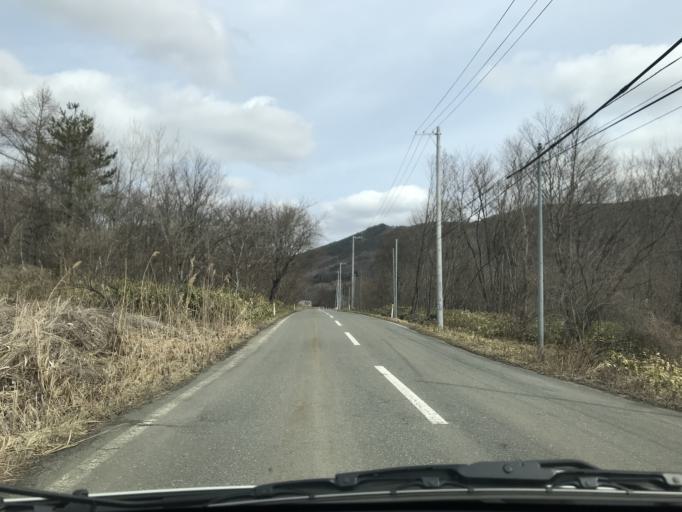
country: JP
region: Iwate
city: Kitakami
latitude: 39.2634
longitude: 141.3176
